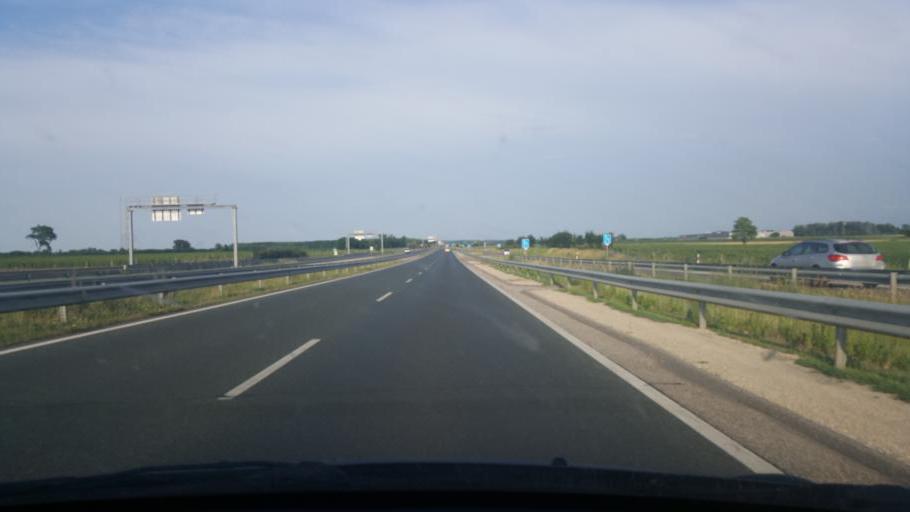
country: HU
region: Pest
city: Vecses
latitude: 47.4041
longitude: 19.3204
